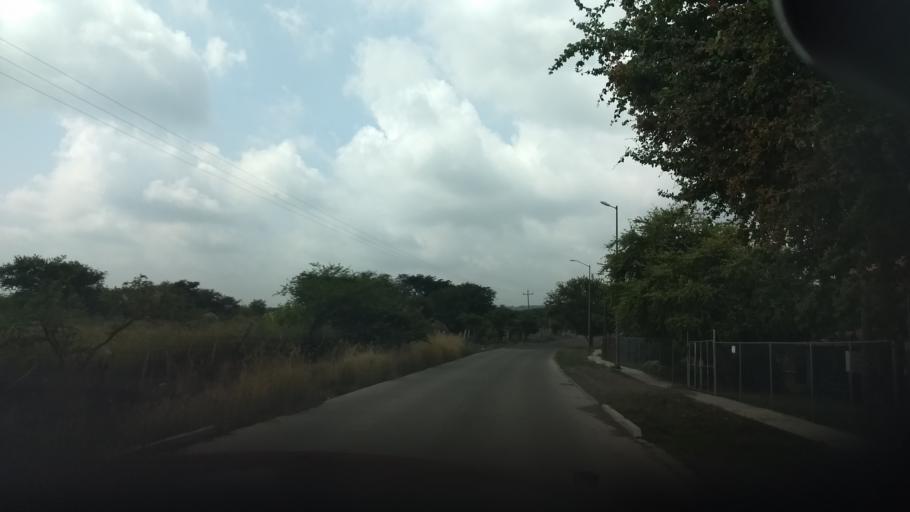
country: MX
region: Jalisco
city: Tonila
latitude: 19.3960
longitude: -103.5311
